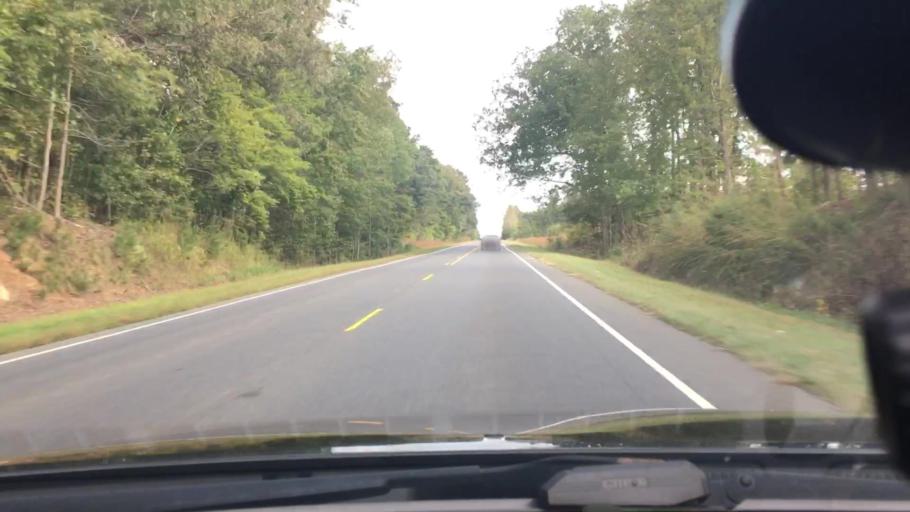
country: US
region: North Carolina
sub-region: Montgomery County
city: Mount Gilead
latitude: 35.3091
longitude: -80.0418
